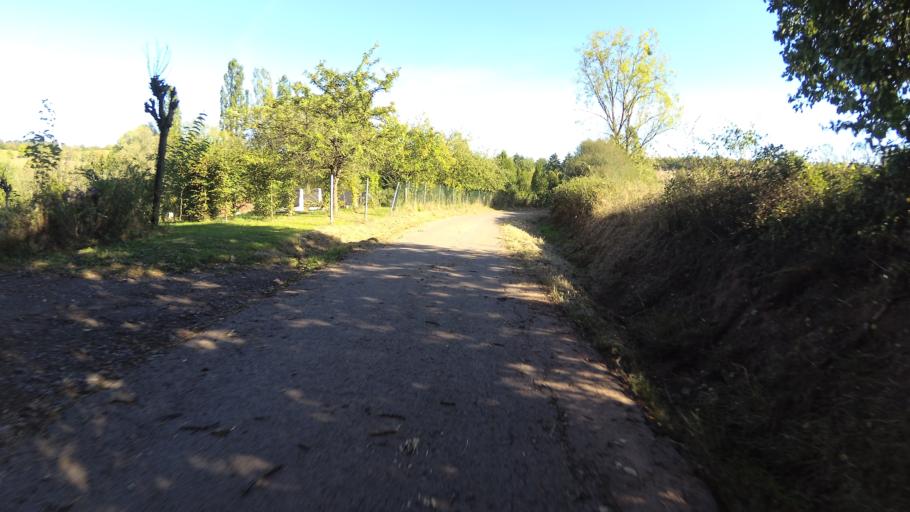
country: DE
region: Saarland
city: Eppelborn
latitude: 49.4249
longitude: 6.9956
